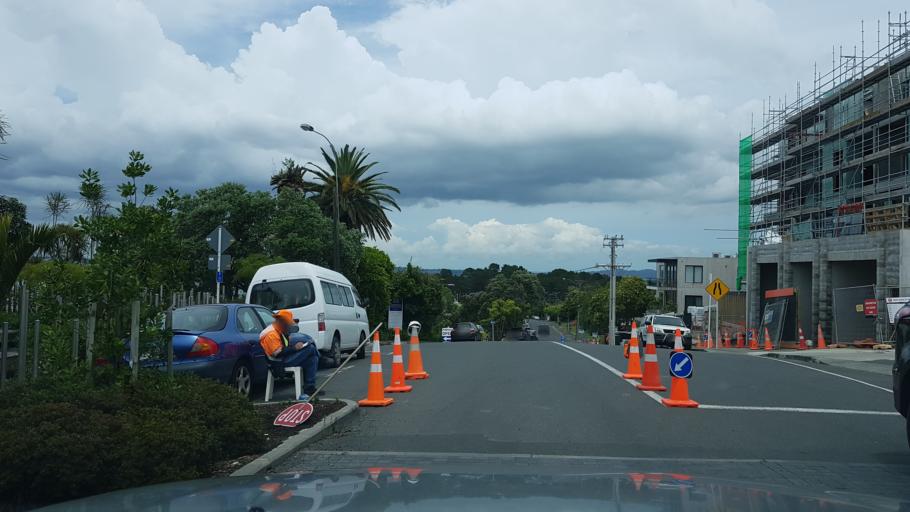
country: NZ
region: Auckland
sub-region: Auckland
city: North Shore
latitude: -36.8129
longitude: 174.7262
